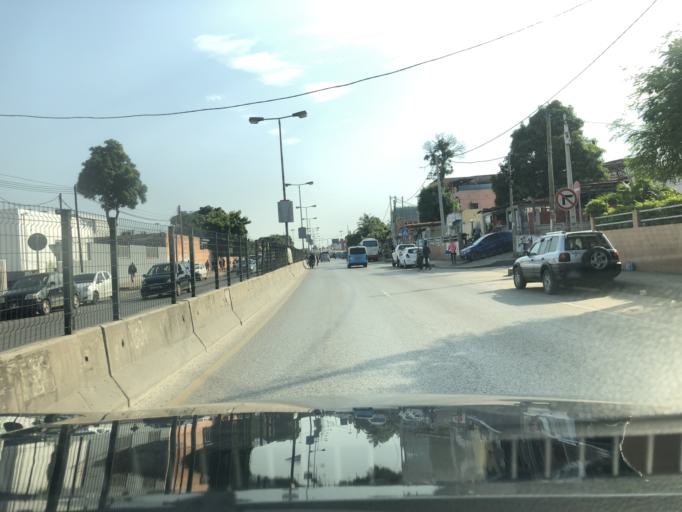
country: AO
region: Luanda
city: Luanda
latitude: -8.8441
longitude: 13.2378
